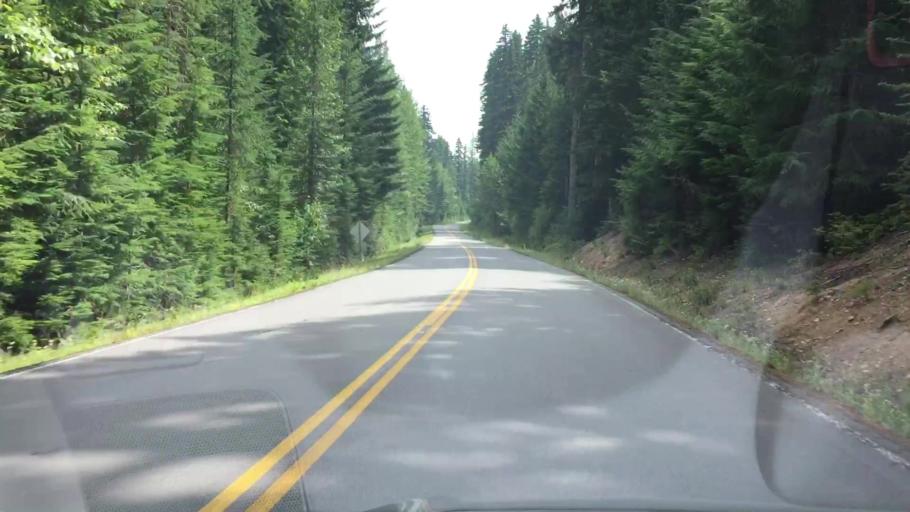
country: US
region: Washington
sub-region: Klickitat County
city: White Salmon
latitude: 46.1322
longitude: -121.6309
